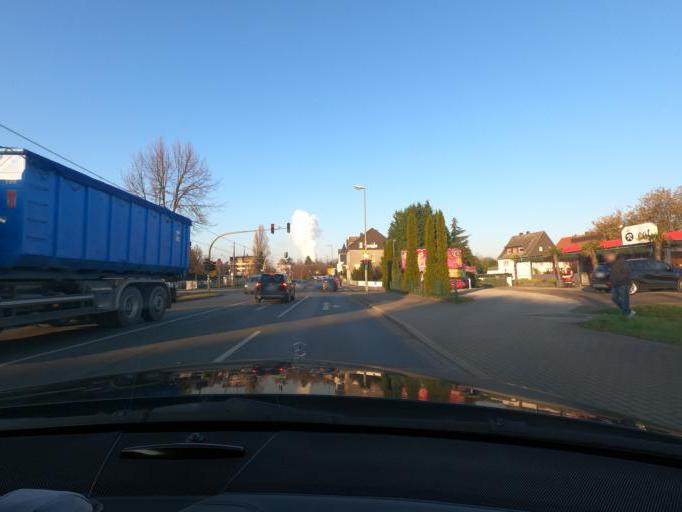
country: DE
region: North Rhine-Westphalia
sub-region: Regierungsbezirk Arnsberg
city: Dortmund
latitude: 51.5793
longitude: 7.4630
